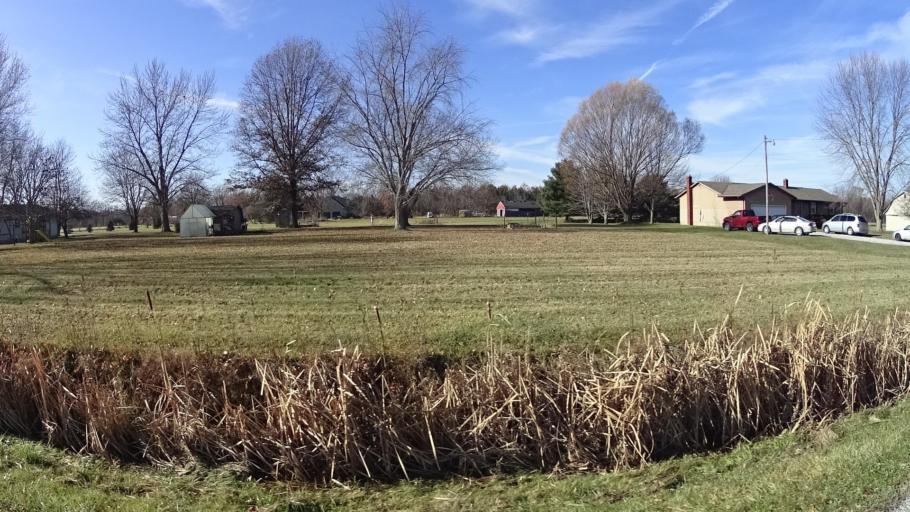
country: US
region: Ohio
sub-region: Lorain County
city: Wellington
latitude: 41.1015
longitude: -82.2007
